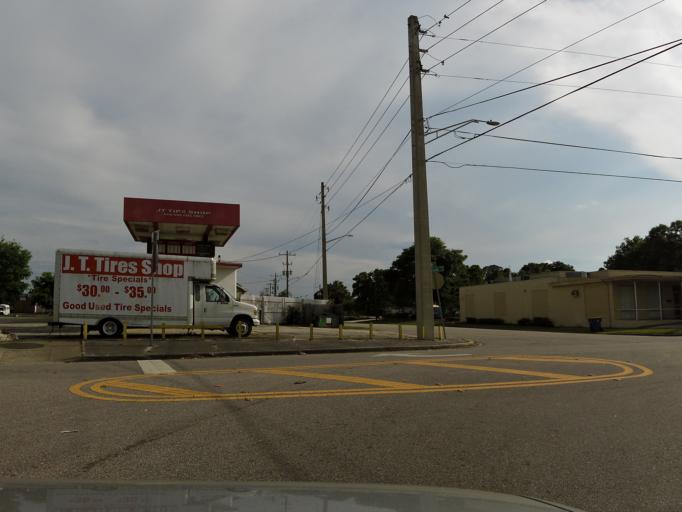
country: US
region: Florida
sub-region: Duval County
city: Jacksonville
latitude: 30.3327
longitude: -81.5890
